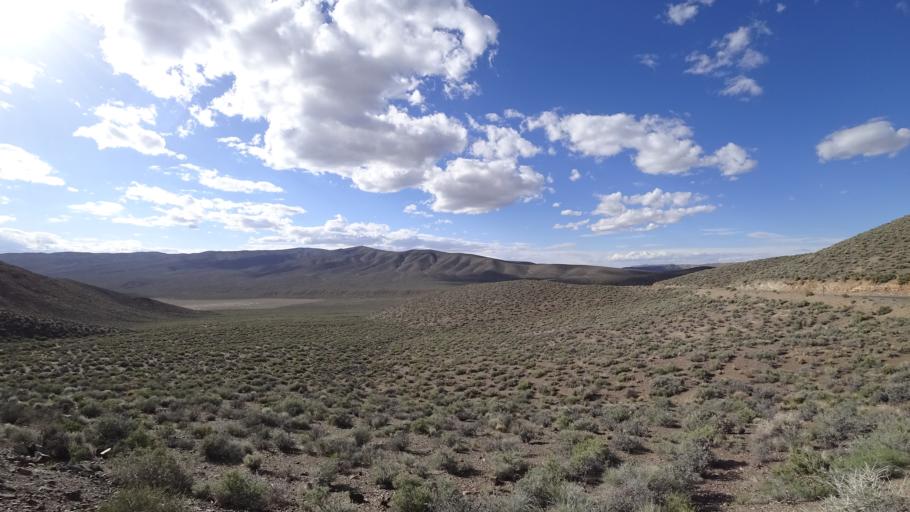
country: US
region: California
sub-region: San Bernardino County
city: Searles Valley
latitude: 36.3211
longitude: -117.1518
